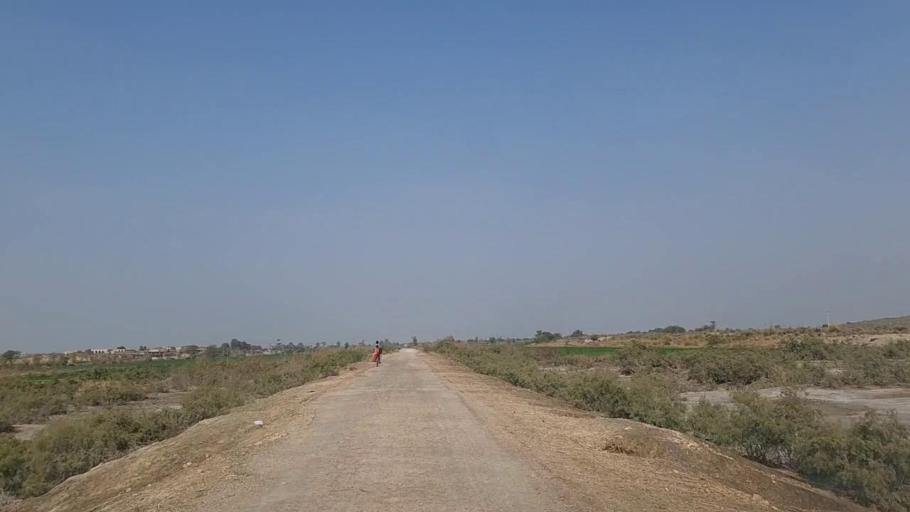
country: PK
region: Sindh
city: Daur
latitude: 26.4773
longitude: 68.4511
